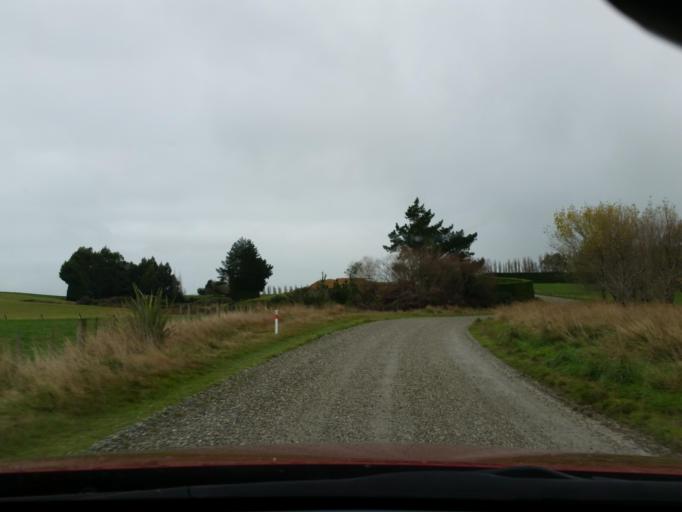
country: NZ
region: Southland
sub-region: Invercargill City
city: Invercargill
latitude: -46.3042
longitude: 168.4795
